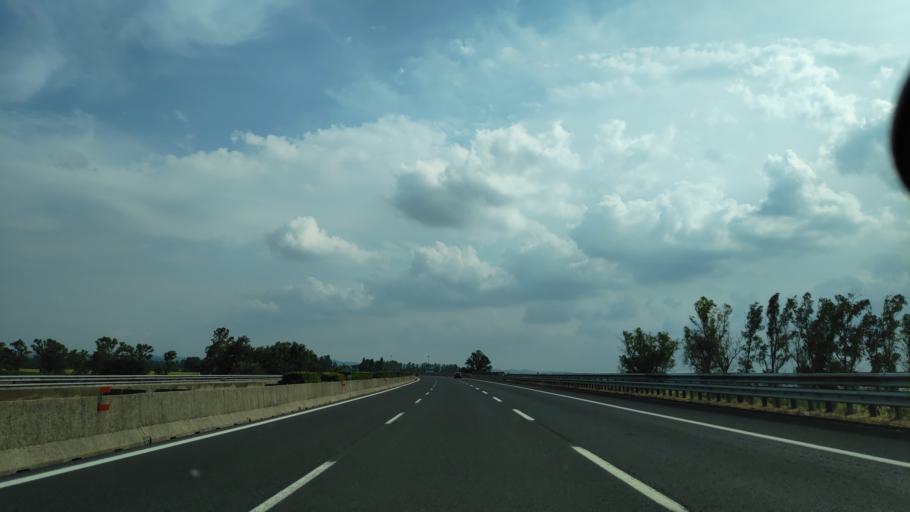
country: IT
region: Latium
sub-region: Citta metropolitana di Roma Capitale
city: Bivio di Capanelle
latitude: 42.1331
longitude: 12.6177
